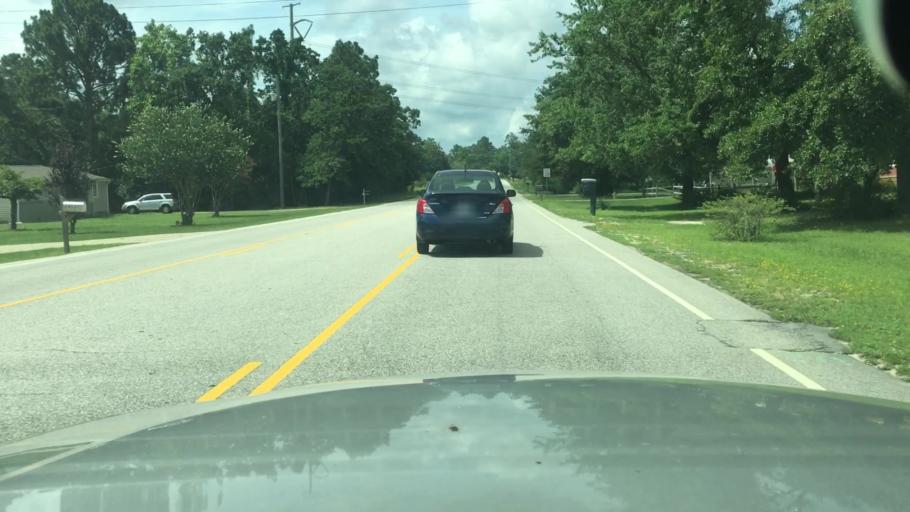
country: US
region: North Carolina
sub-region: Cumberland County
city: Hope Mills
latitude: 35.0224
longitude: -78.9328
